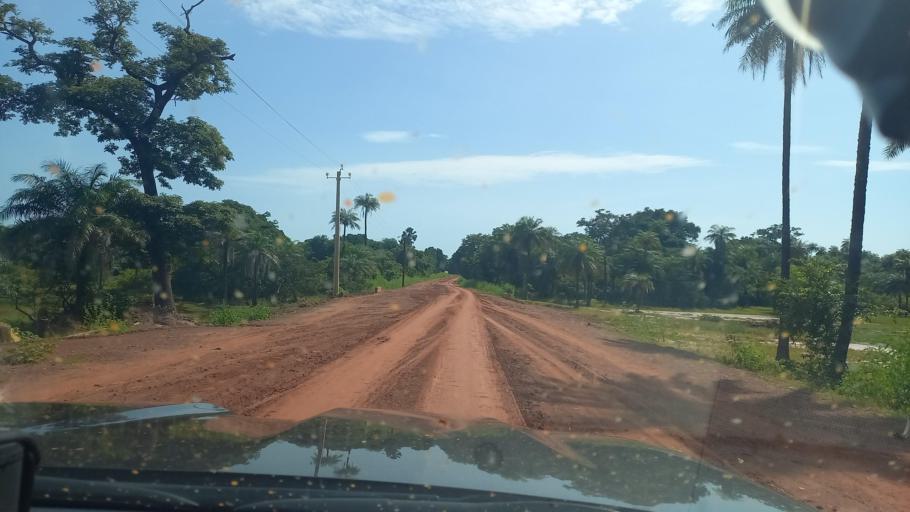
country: SN
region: Ziguinchor
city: Adeane
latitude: 12.6673
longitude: -16.1010
